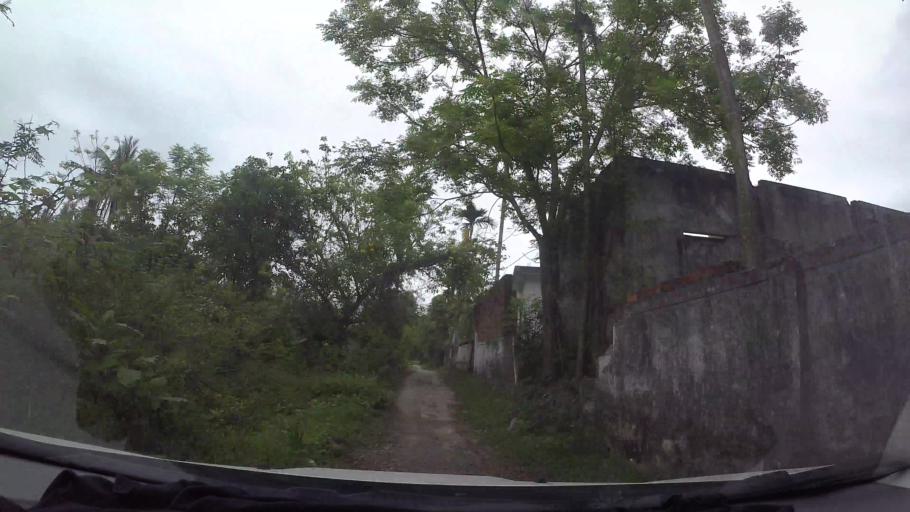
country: VN
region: Da Nang
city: Lien Chieu
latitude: 16.0965
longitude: 108.1040
